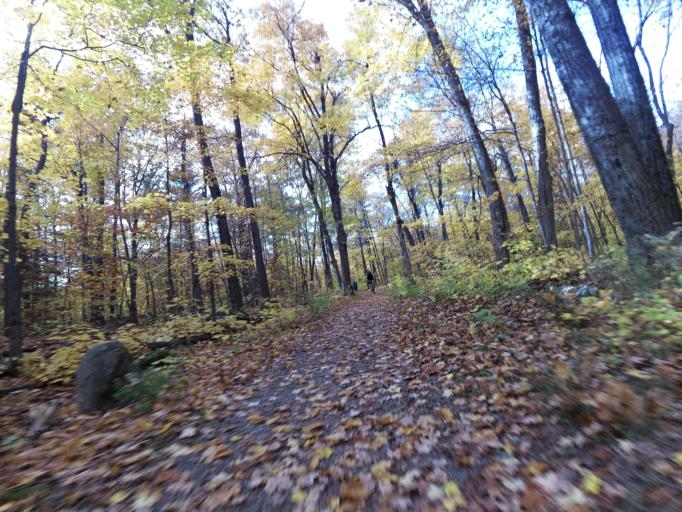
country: CA
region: Quebec
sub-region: Outaouais
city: Gatineau
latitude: 45.4811
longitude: -75.8401
